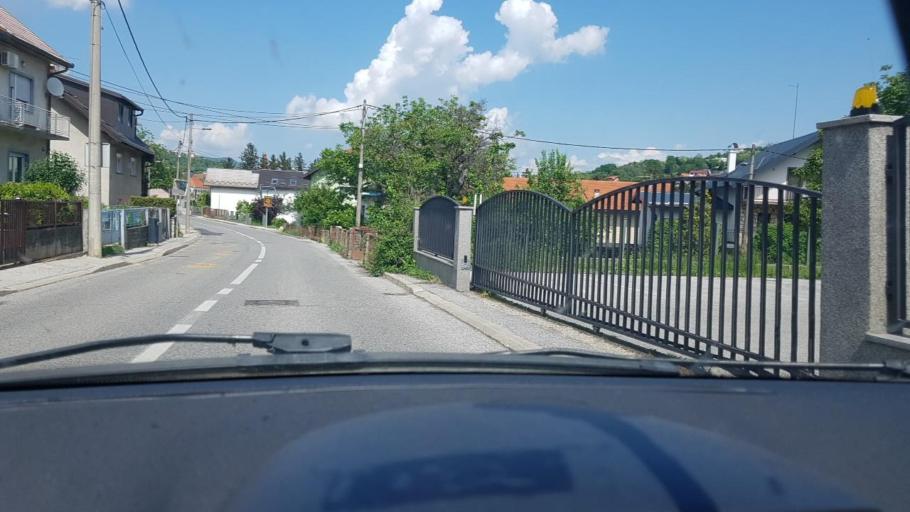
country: HR
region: Grad Zagreb
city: Kasina
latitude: 45.8731
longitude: 16.0109
